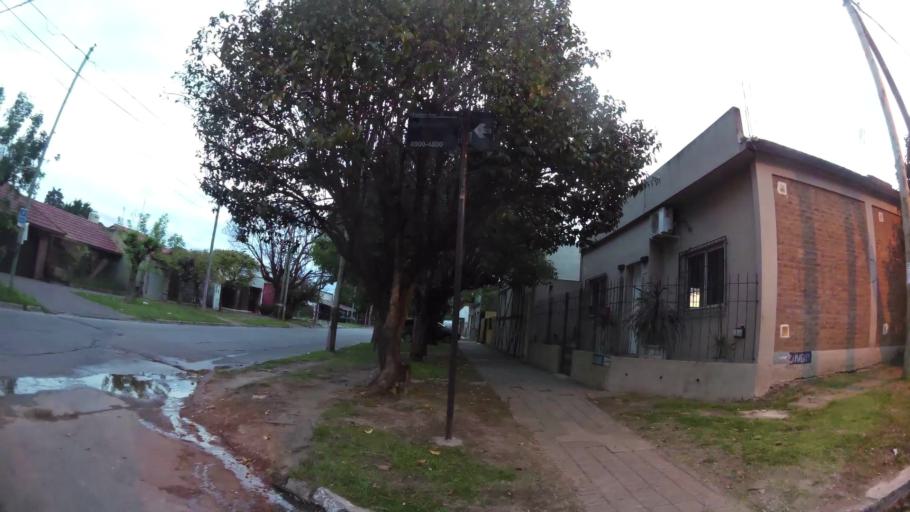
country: AR
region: Buenos Aires
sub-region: Partido de Quilmes
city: Quilmes
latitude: -34.7448
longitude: -58.2309
